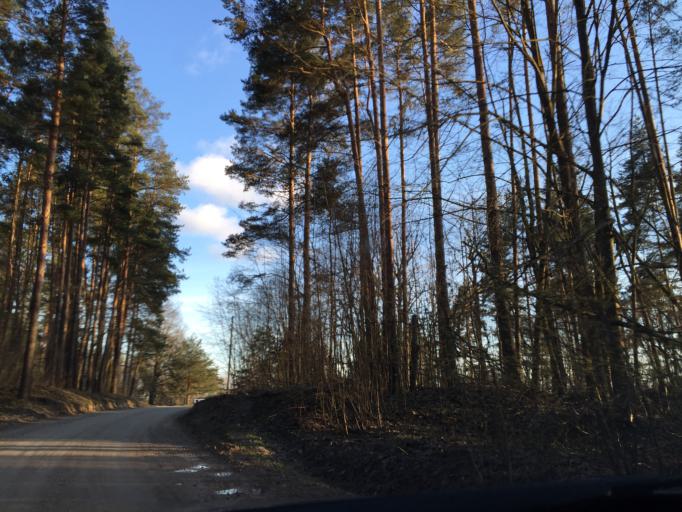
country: LV
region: Kekava
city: Kekava
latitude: 56.8517
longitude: 24.2245
